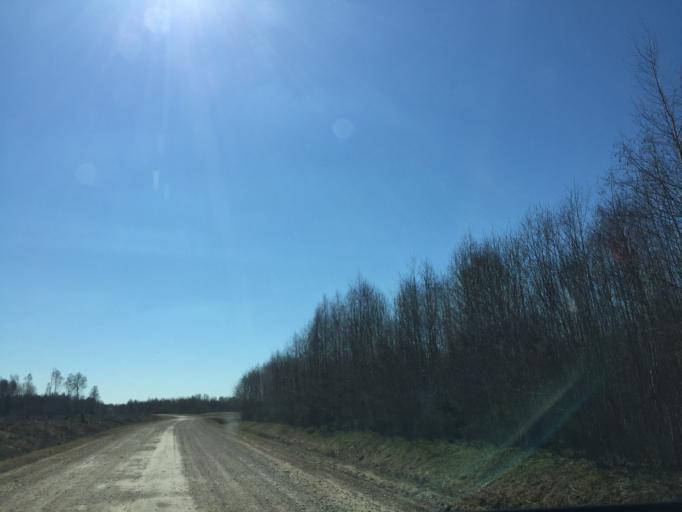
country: EE
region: Viljandimaa
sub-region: Viiratsi vald
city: Viiratsi
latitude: 58.4033
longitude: 25.8710
